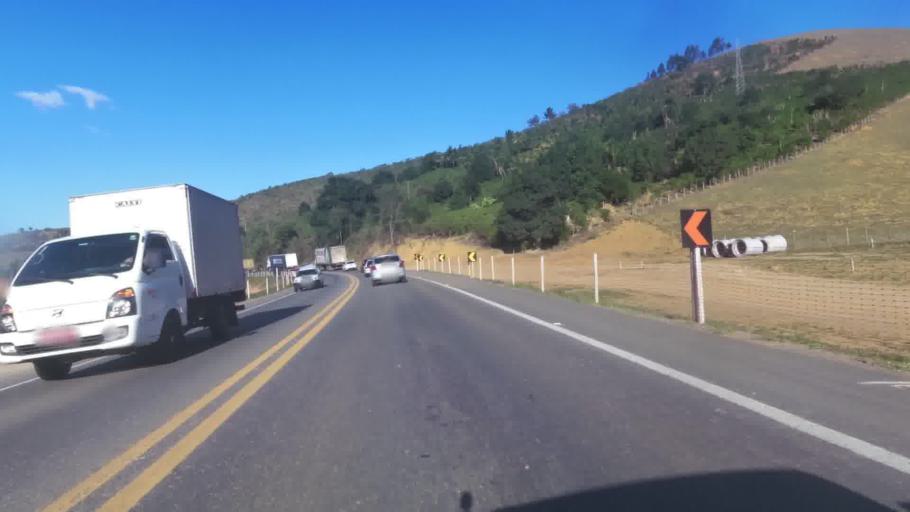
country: BR
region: Espirito Santo
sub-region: Iconha
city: Iconha
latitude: -20.7347
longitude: -40.7539
